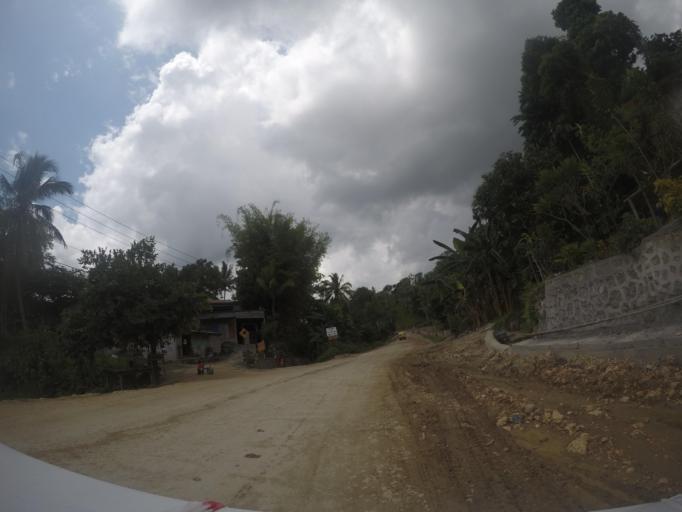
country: TL
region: Baucau
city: Venilale
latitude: -8.6005
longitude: 126.3858
